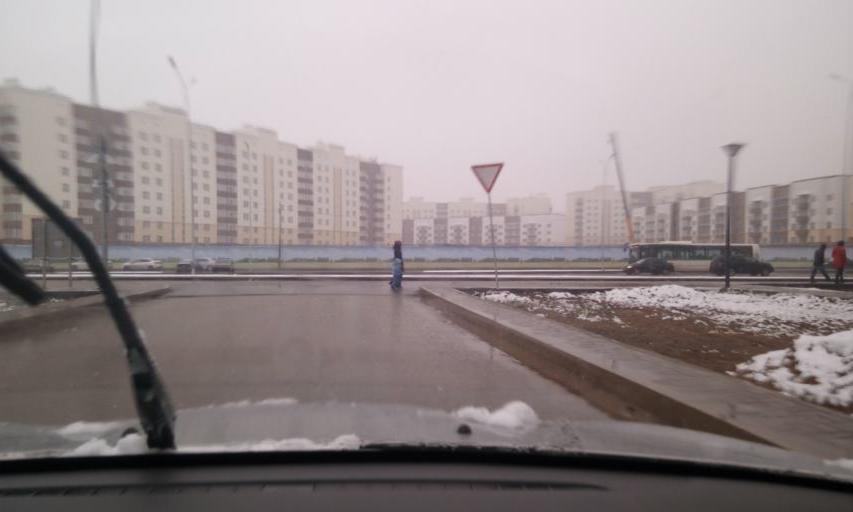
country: KZ
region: Astana Qalasy
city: Astana
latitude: 51.1253
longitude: 71.5008
